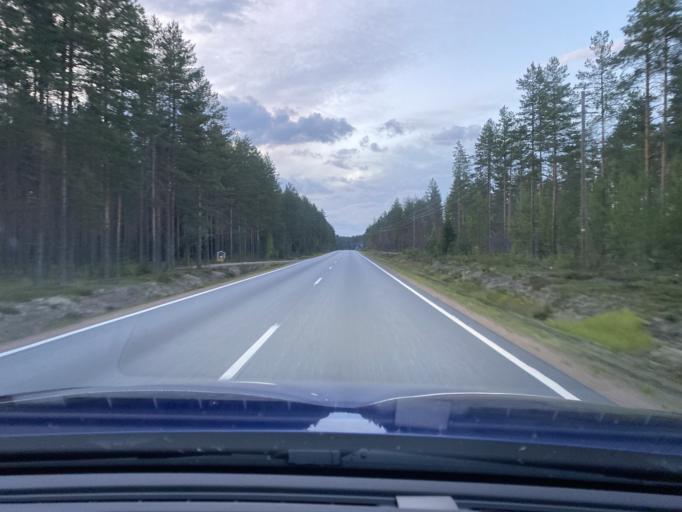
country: FI
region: Satakunta
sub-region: Pohjois-Satakunta
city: Honkajoki
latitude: 62.2041
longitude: 22.2995
